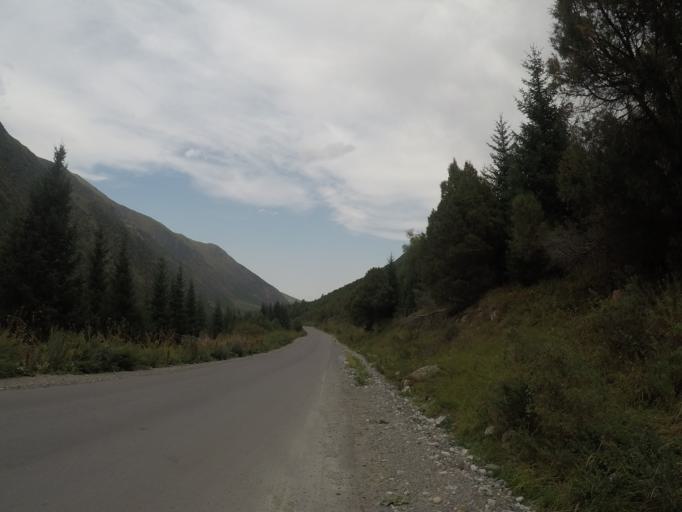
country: KG
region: Chuy
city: Bishkek
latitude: 42.5855
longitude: 74.4839
